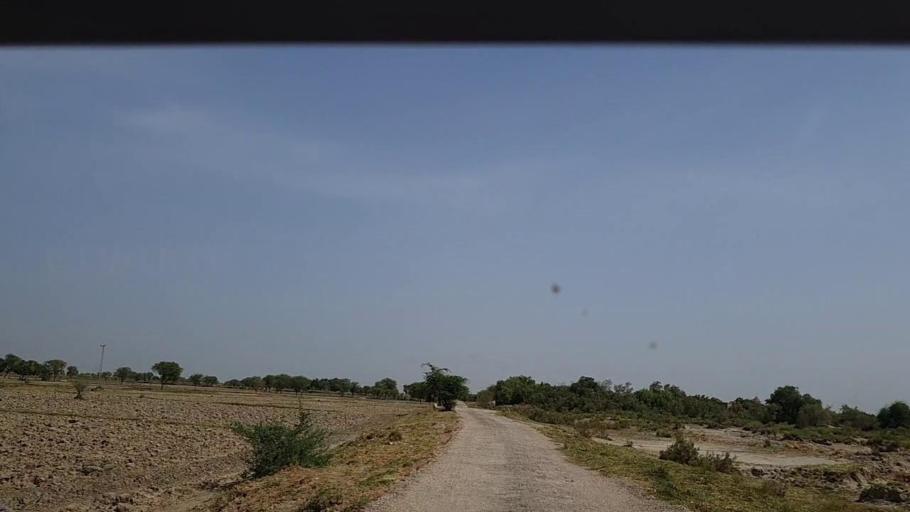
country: PK
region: Sindh
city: Phulji
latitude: 26.9474
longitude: 67.7160
